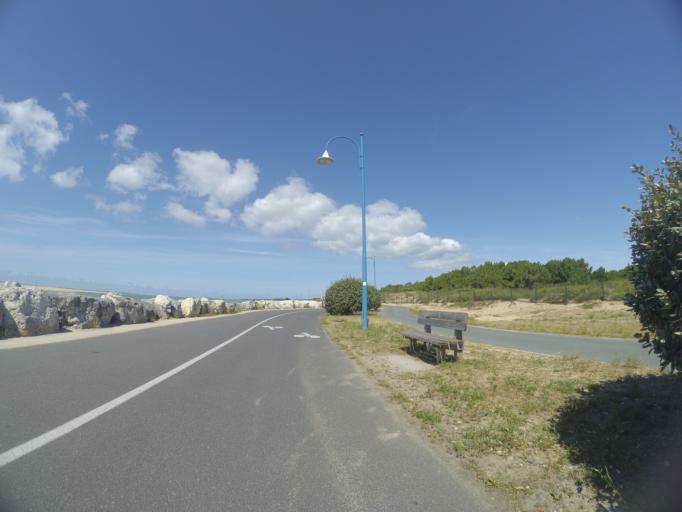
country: FR
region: Poitou-Charentes
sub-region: Departement de la Charente-Maritime
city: Les Mathes
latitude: 45.6770
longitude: -1.1695
